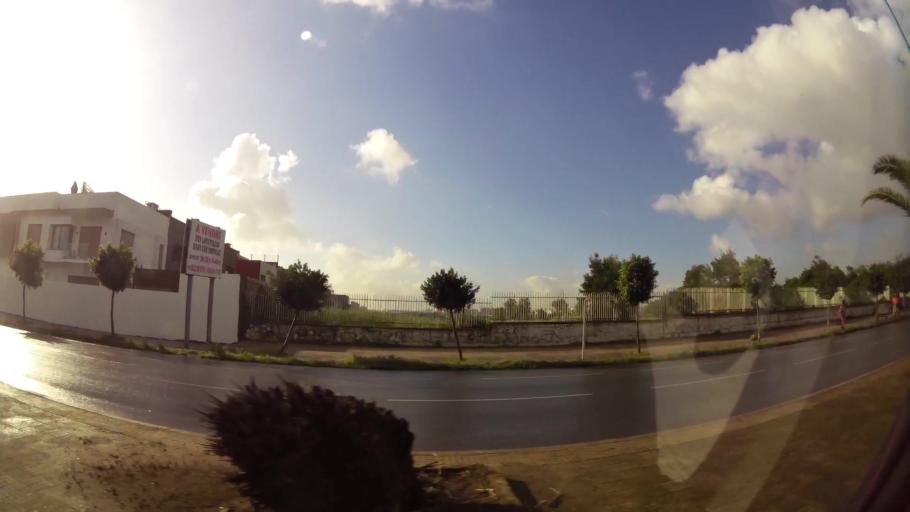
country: MA
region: Grand Casablanca
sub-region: Mediouna
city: Tit Mellil
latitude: 33.5958
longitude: -7.5259
